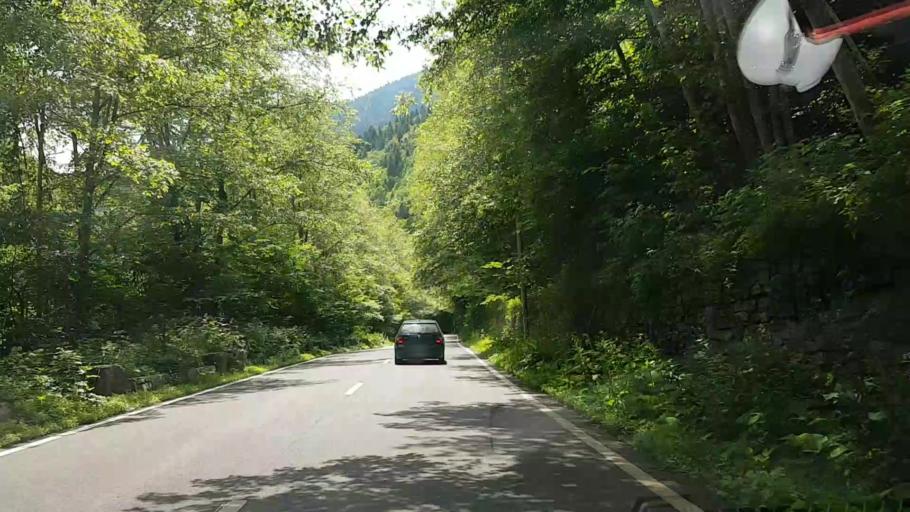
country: RO
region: Suceava
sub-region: Comuna Crucea
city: Crucea
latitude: 47.2959
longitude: 25.6323
